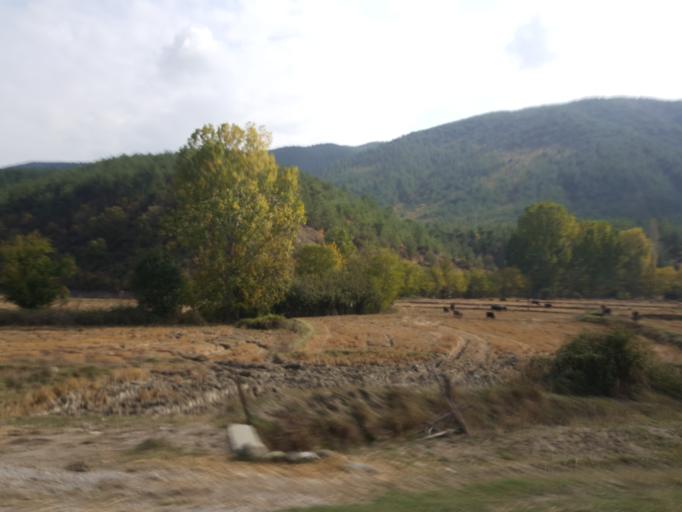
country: TR
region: Sinop
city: Duragan
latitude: 41.3904
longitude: 34.9458
